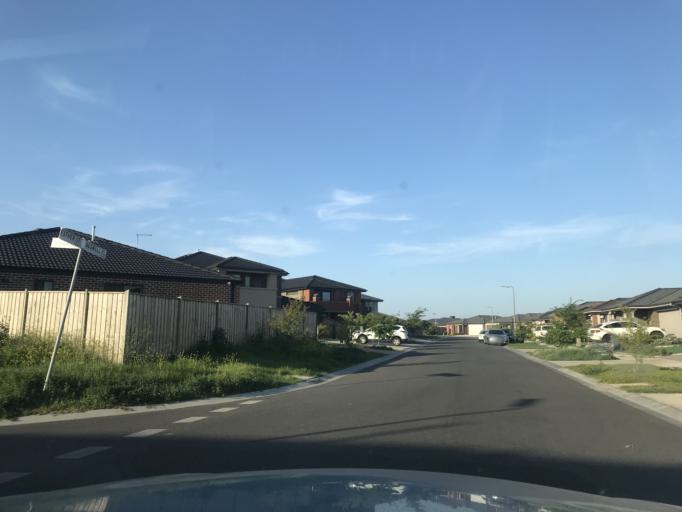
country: AU
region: Victoria
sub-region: Wyndham
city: Williams Landing
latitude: -37.8602
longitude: 144.7254
